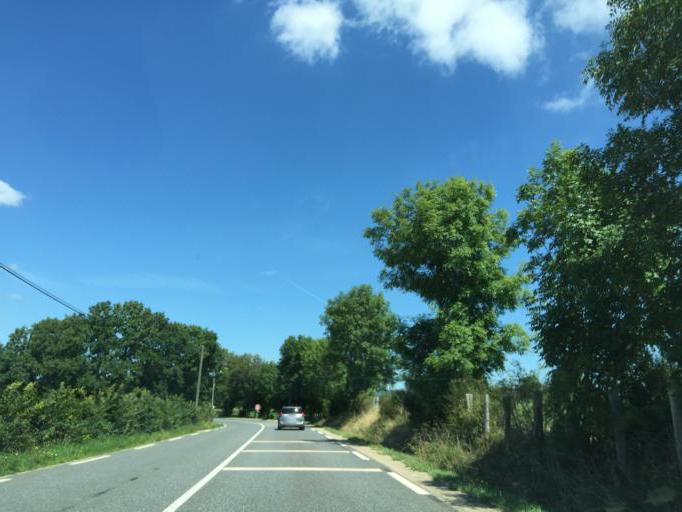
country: FR
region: Midi-Pyrenees
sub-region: Departement de l'Aveyron
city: Laguiole
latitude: 44.6085
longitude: 2.8050
